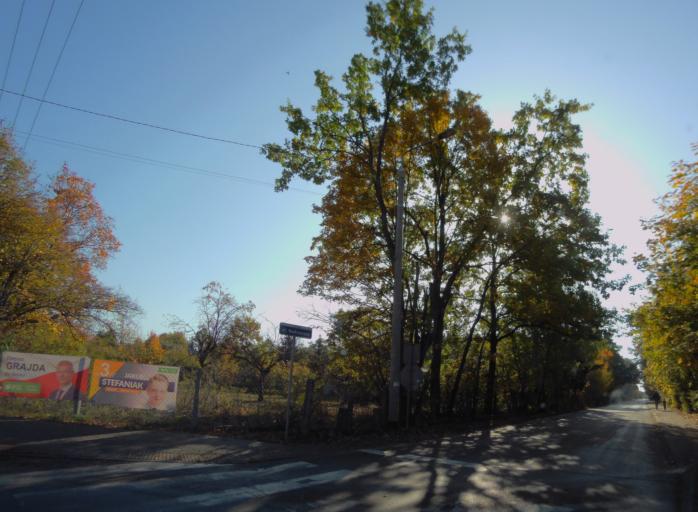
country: PL
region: Masovian Voivodeship
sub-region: Powiat otwocki
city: Jozefow
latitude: 52.1712
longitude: 21.3012
